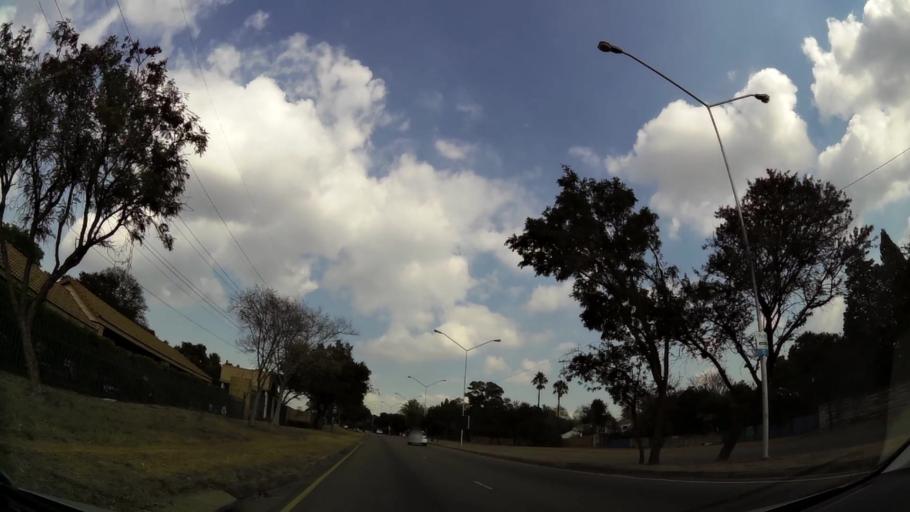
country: ZA
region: Gauteng
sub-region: City of Tshwane Metropolitan Municipality
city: Pretoria
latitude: -25.7803
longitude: 28.2878
